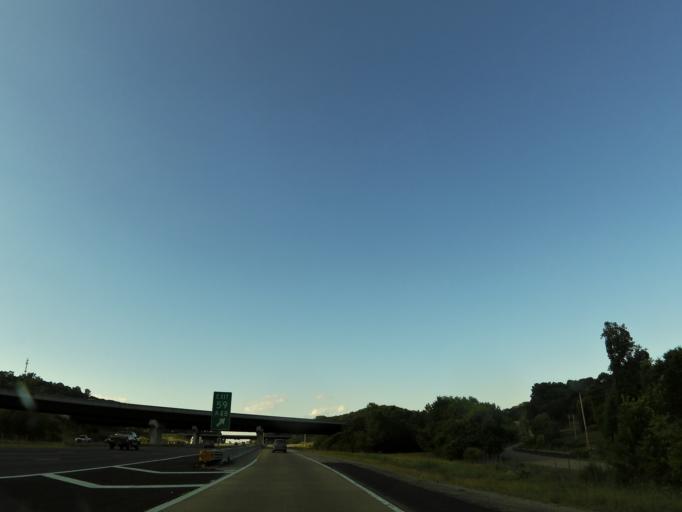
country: US
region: Tennessee
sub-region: Williamson County
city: Thompson's Station
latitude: 35.8174
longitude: -86.8414
